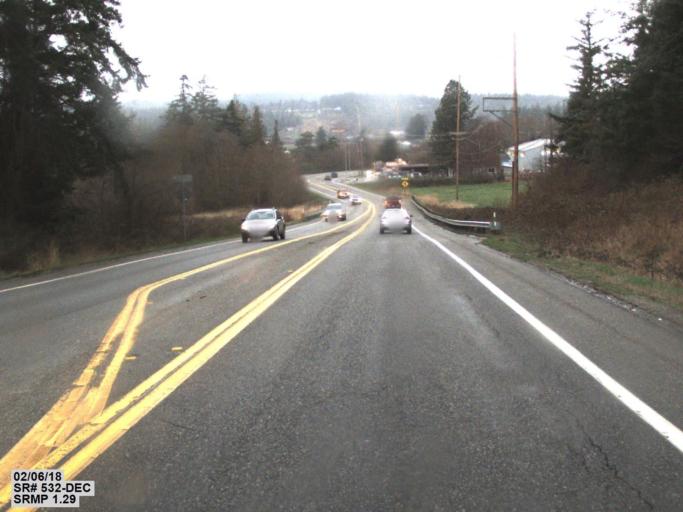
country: US
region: Washington
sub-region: Snohomish County
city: Stanwood
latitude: 48.2399
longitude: -122.4294
